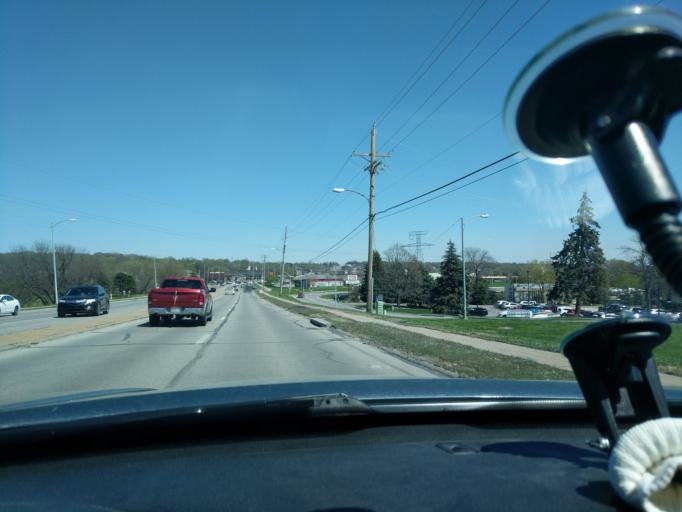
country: US
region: Nebraska
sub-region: Douglas County
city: Ralston
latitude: 41.2335
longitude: -96.0579
